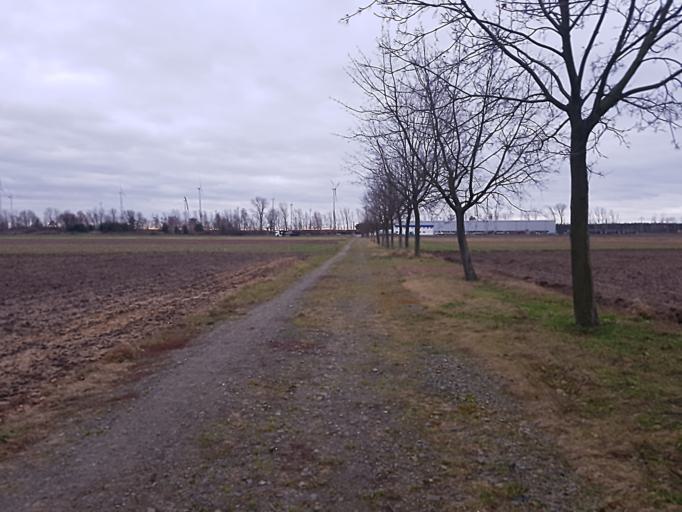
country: DE
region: Brandenburg
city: Falkenberg
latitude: 51.5890
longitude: 13.2847
